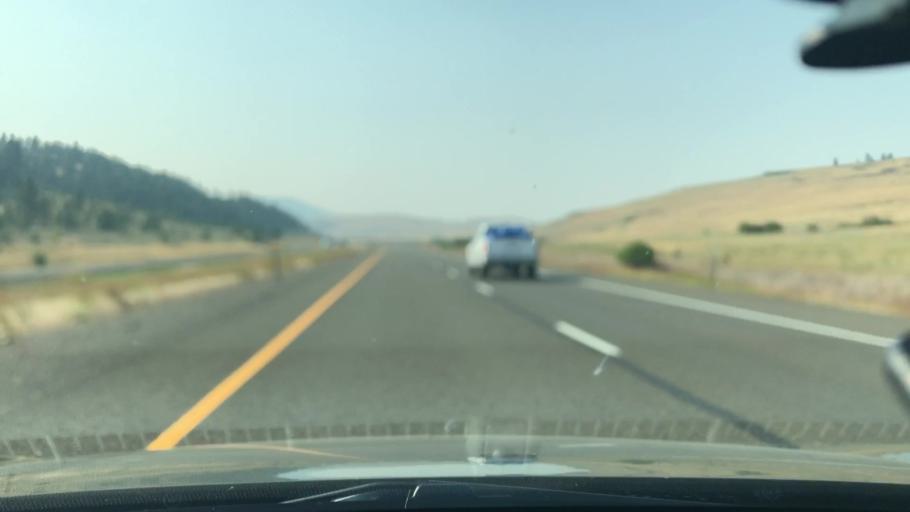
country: US
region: Oregon
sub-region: Union County
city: Union
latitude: 45.1773
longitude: -117.9810
